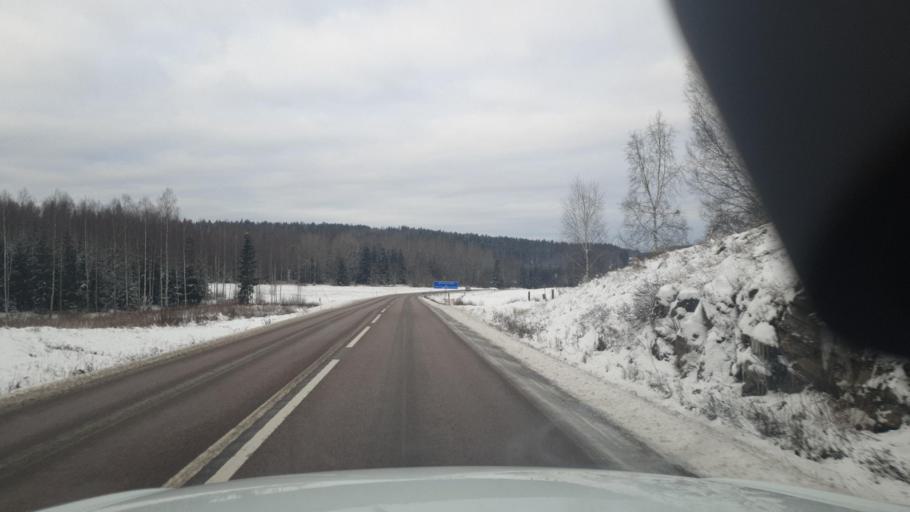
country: SE
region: Vaermland
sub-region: Karlstads Kommun
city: Edsvalla
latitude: 59.5296
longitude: 13.1202
